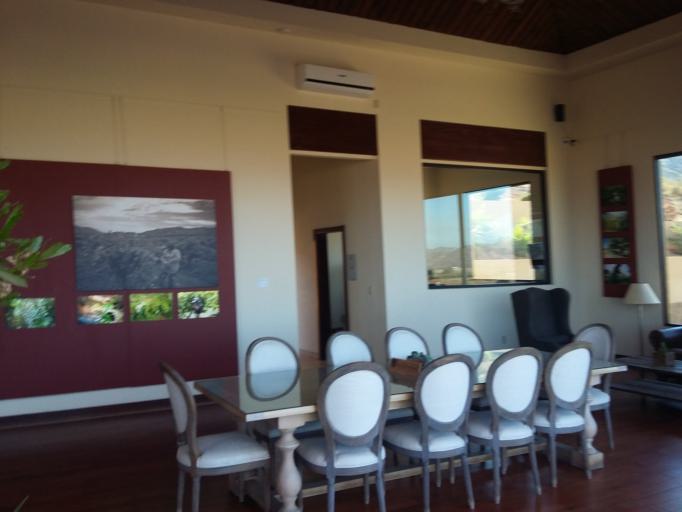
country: MX
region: Baja California
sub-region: Ensenada
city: Rancho Verde
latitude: 32.0801
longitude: -116.6543
